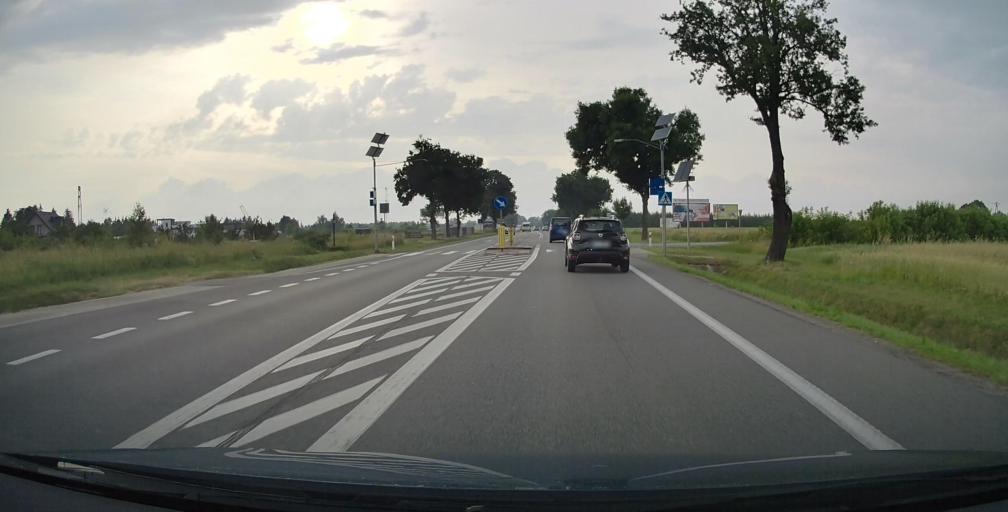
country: PL
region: Masovian Voivodeship
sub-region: Siedlce
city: Siedlce
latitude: 52.1301
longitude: 22.3342
